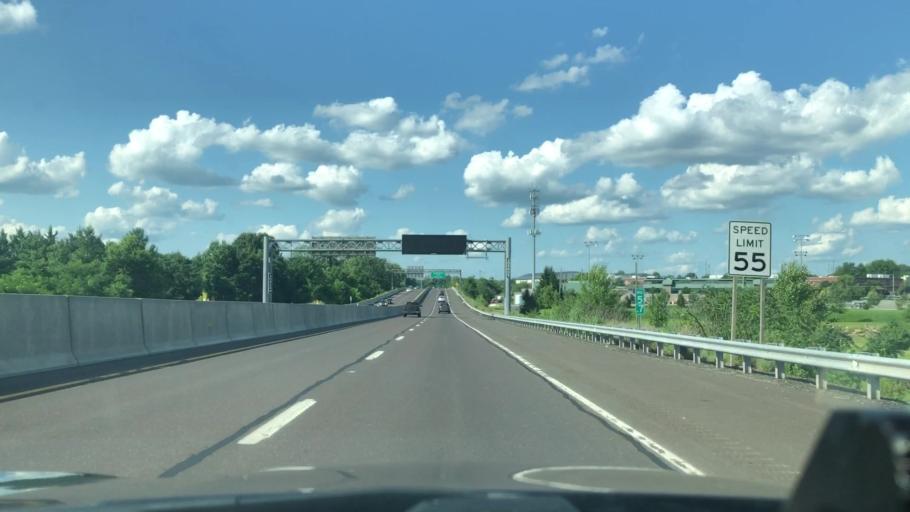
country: US
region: Pennsylvania
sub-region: Montgomery County
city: Fort Washington
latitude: 40.1492
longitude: -75.2037
